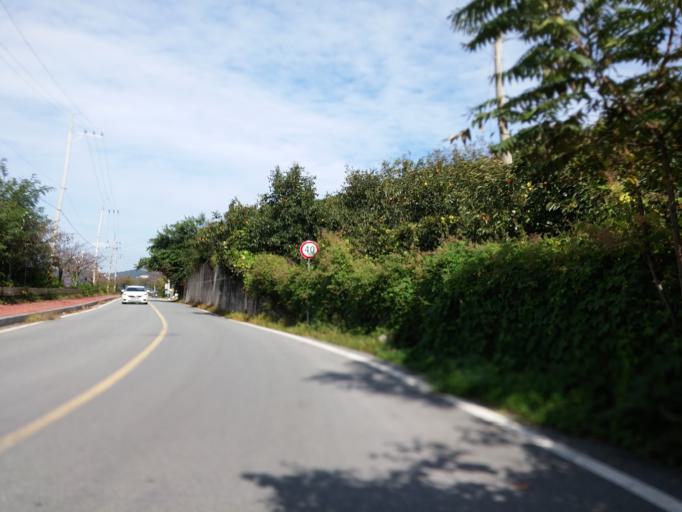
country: KR
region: Chungcheongnam-do
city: Yonmu
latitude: 36.1758
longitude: 127.1544
